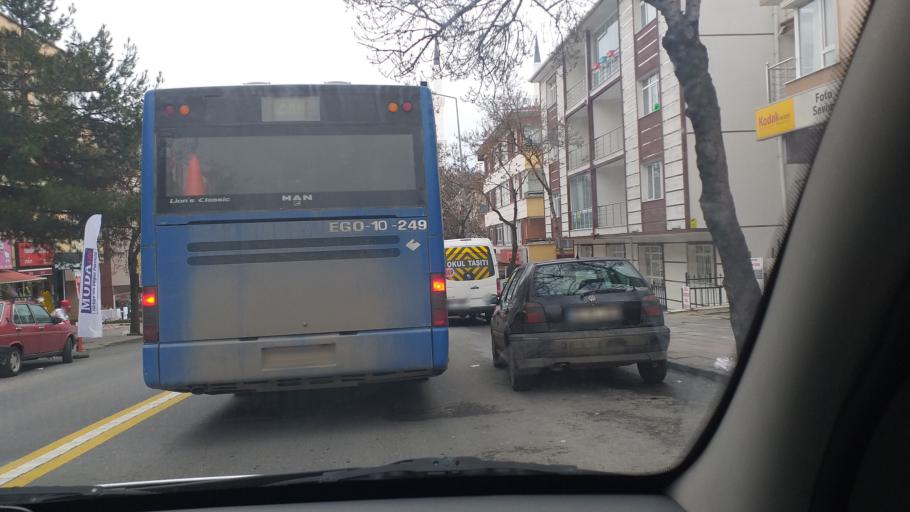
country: TR
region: Ankara
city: Ankara
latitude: 39.9752
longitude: 32.8411
